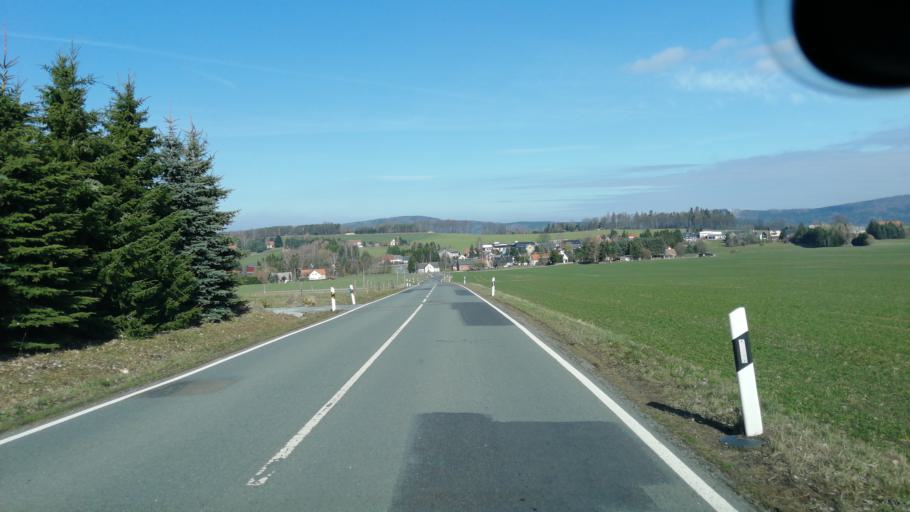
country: DE
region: Saxony
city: Beiersdorf
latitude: 51.0716
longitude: 14.5498
